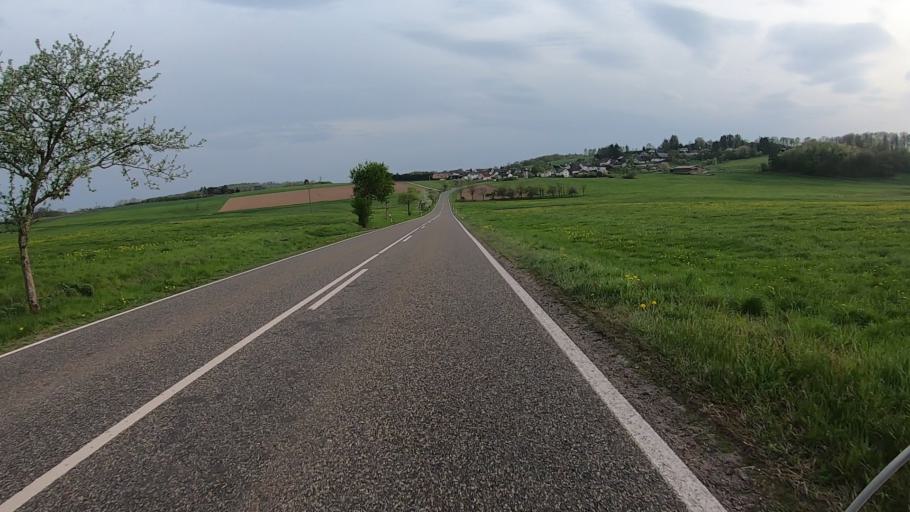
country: DE
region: Rheinland-Pfalz
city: Niedersayn
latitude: 50.5397
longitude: 7.8311
